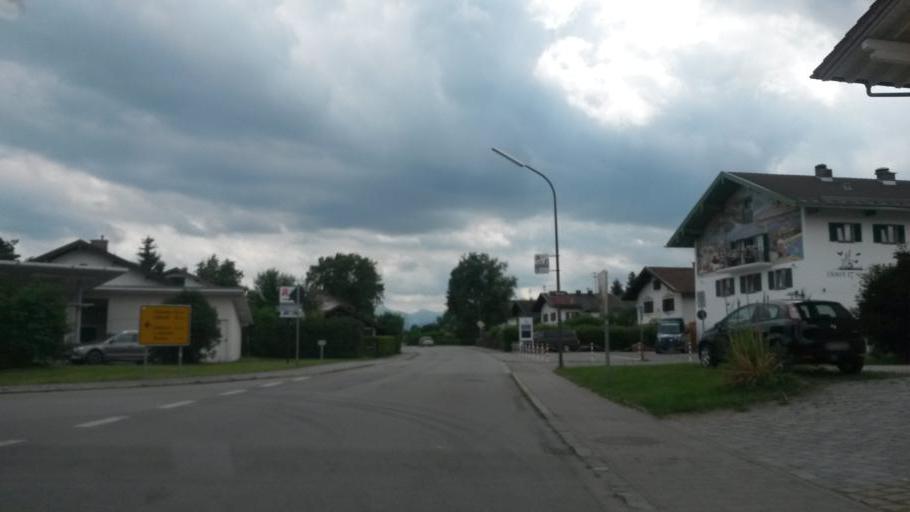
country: DE
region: Bavaria
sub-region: Upper Bavaria
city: Eggstatt
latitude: 47.9225
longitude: 12.3808
